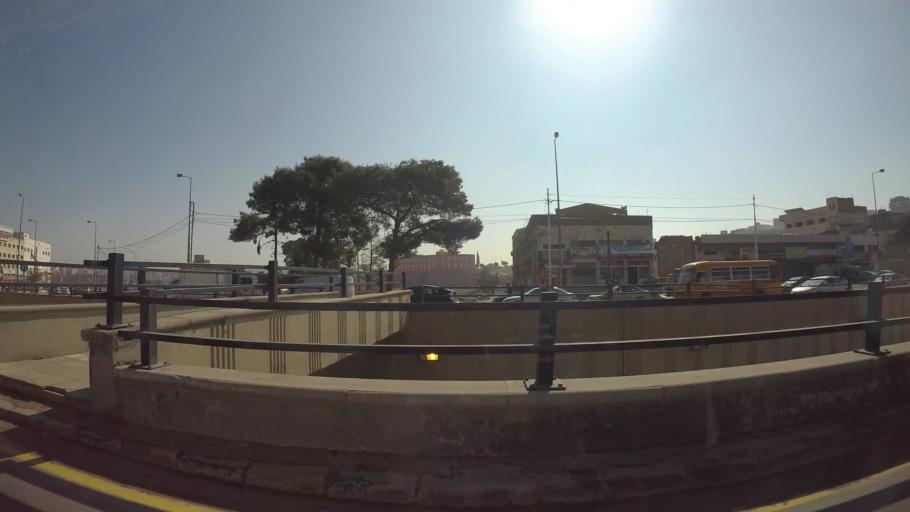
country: JO
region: Amman
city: Al Bunayyat ash Shamaliyah
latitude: 31.9163
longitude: 35.9026
